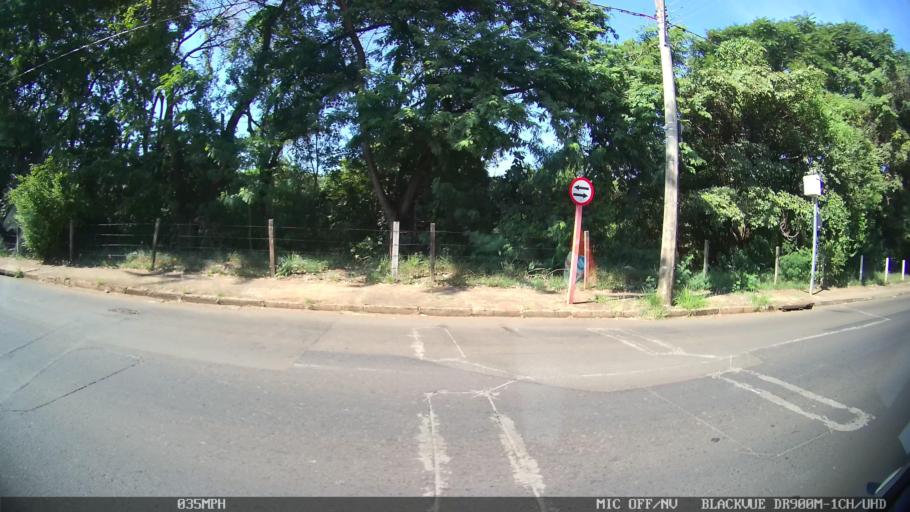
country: BR
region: Sao Paulo
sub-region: Sao Jose Do Rio Preto
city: Sao Jose do Rio Preto
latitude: -20.7863
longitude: -49.3856
